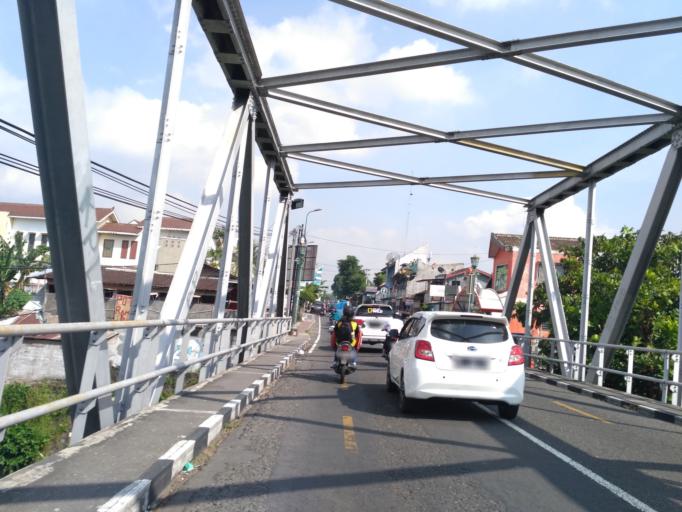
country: ID
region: Daerah Istimewa Yogyakarta
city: Yogyakarta
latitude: -7.7785
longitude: 110.3705
